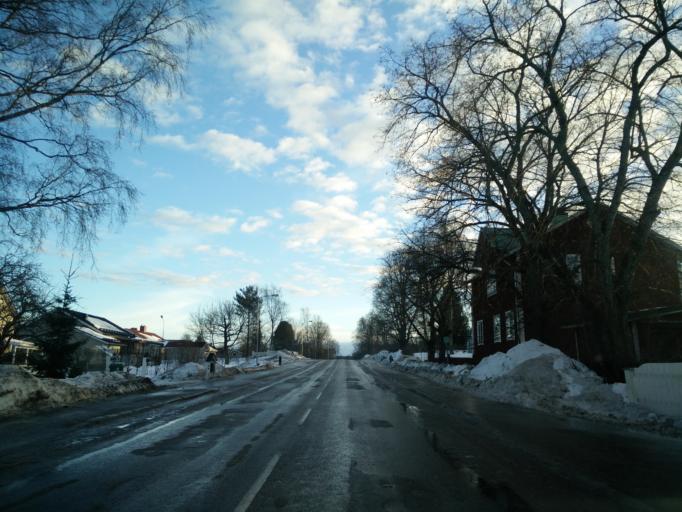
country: SE
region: Vaesternorrland
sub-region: Sundsvalls Kommun
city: Njurundabommen
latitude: 62.2621
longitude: 17.3766
